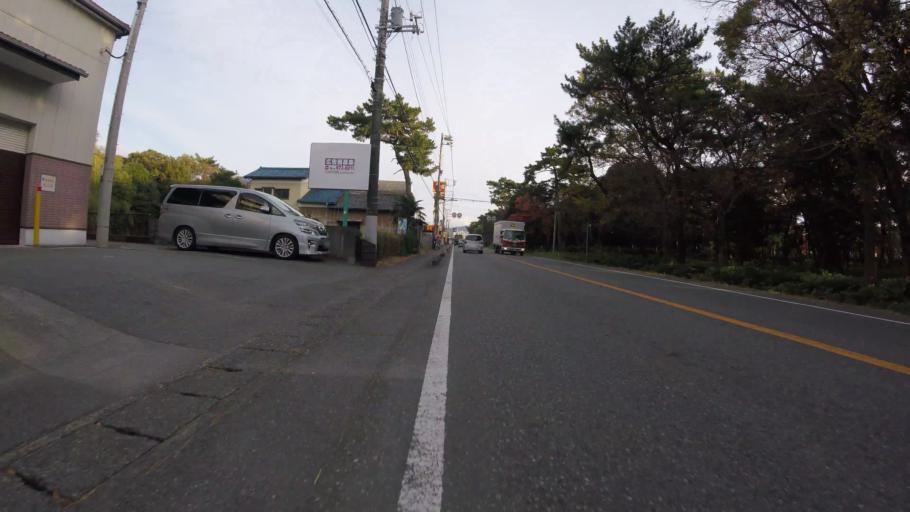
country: JP
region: Shizuoka
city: Numazu
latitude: 35.1066
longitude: 138.8342
